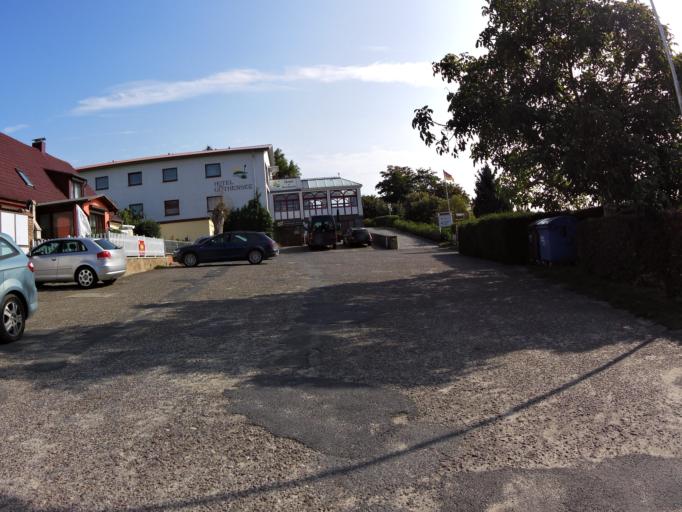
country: DE
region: Mecklenburg-Vorpommern
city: Seebad Bansin
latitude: 53.9568
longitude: 14.1431
